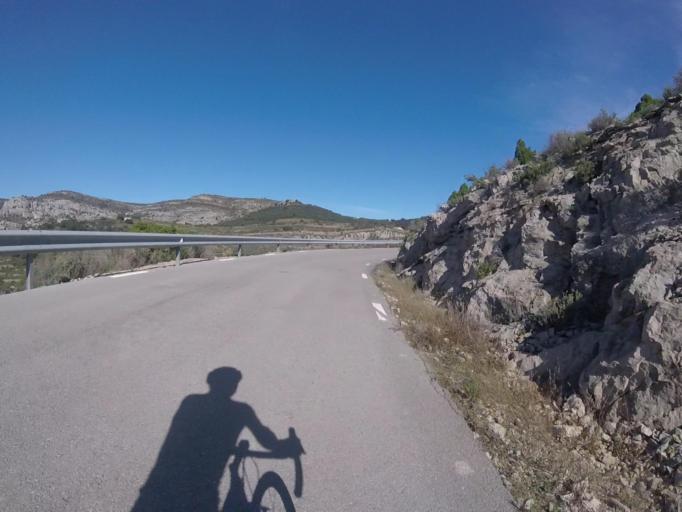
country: ES
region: Valencia
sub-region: Provincia de Castello
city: Sarratella
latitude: 40.2964
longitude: 0.0270
